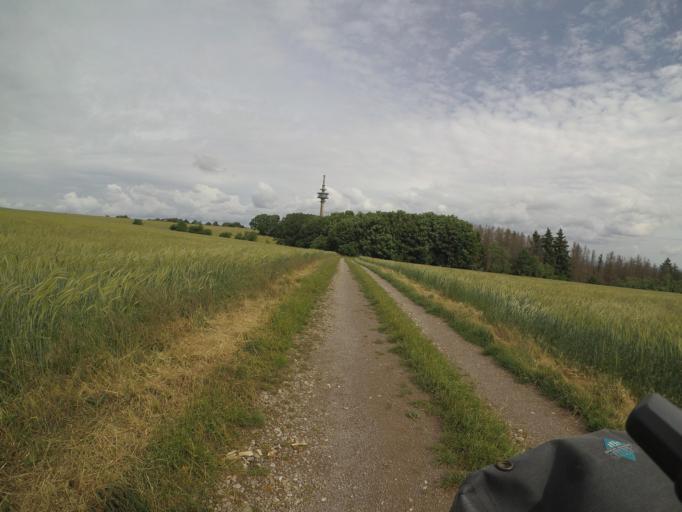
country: DE
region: North Rhine-Westphalia
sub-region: Regierungsbezirk Koln
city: Hurtgenwald
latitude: 50.7323
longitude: 6.4070
